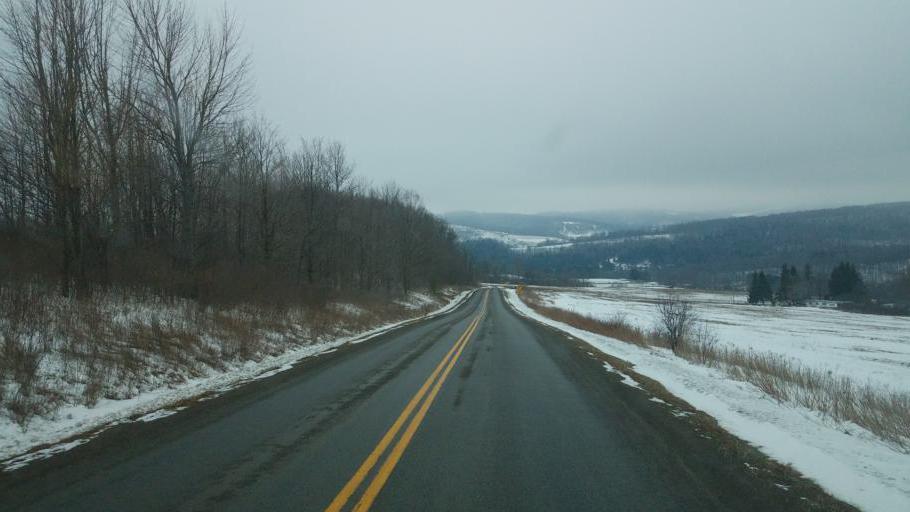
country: US
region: Pennsylvania
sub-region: Tioga County
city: Westfield
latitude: 42.0466
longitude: -77.5376
